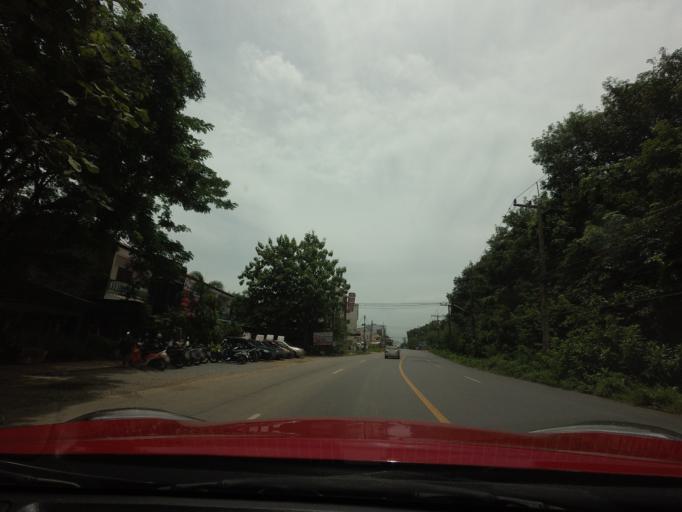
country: TH
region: Songkhla
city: Hat Yai
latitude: 6.9977
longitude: 100.5111
